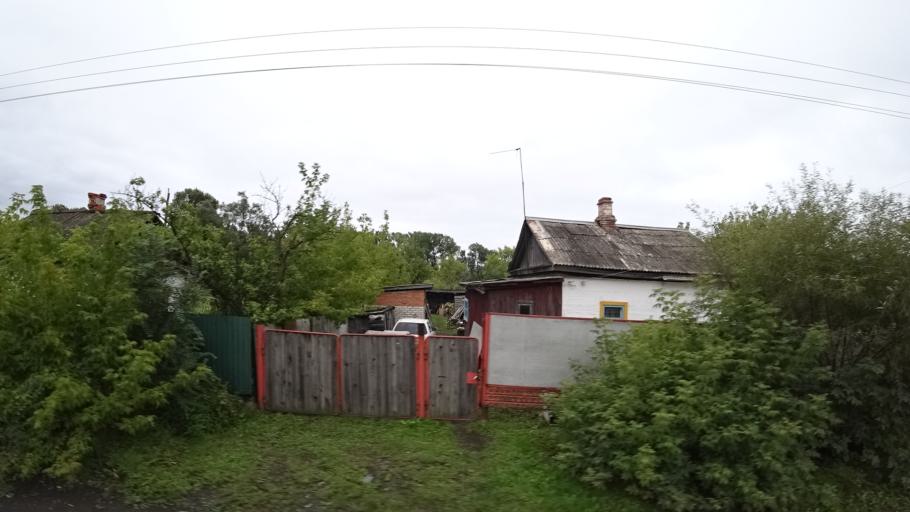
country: RU
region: Primorskiy
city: Chernigovka
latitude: 44.3346
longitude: 132.5319
